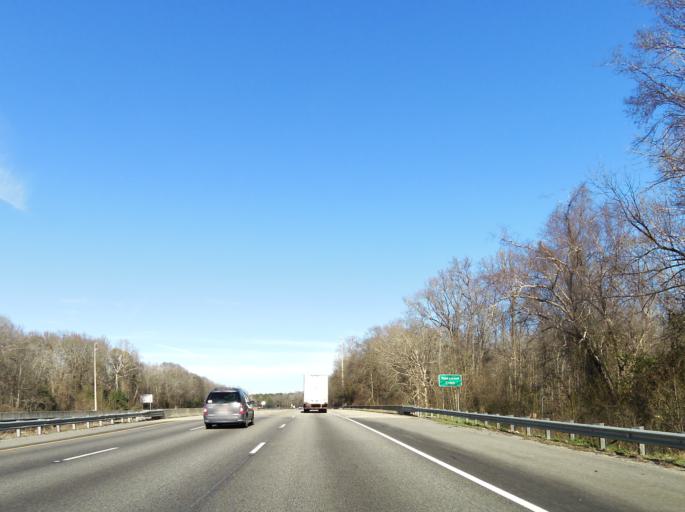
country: US
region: Georgia
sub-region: Bibb County
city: West Point
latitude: 32.7645
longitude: -83.7104
